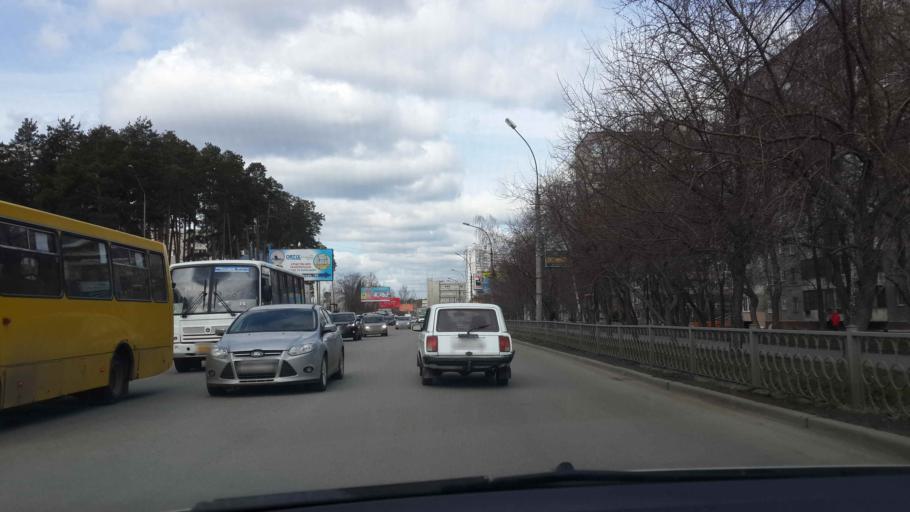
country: RU
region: Sverdlovsk
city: Sovkhoznyy
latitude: 56.8101
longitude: 60.5638
